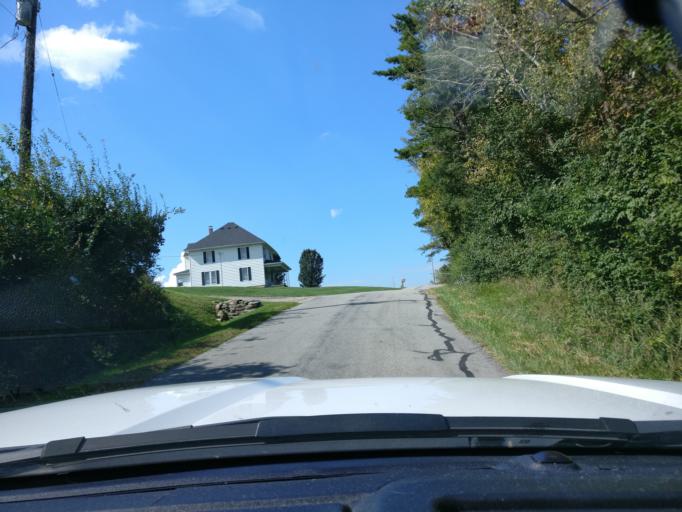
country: US
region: Ohio
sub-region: Clinton County
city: Wilmington
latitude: 39.4625
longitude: -83.9560
